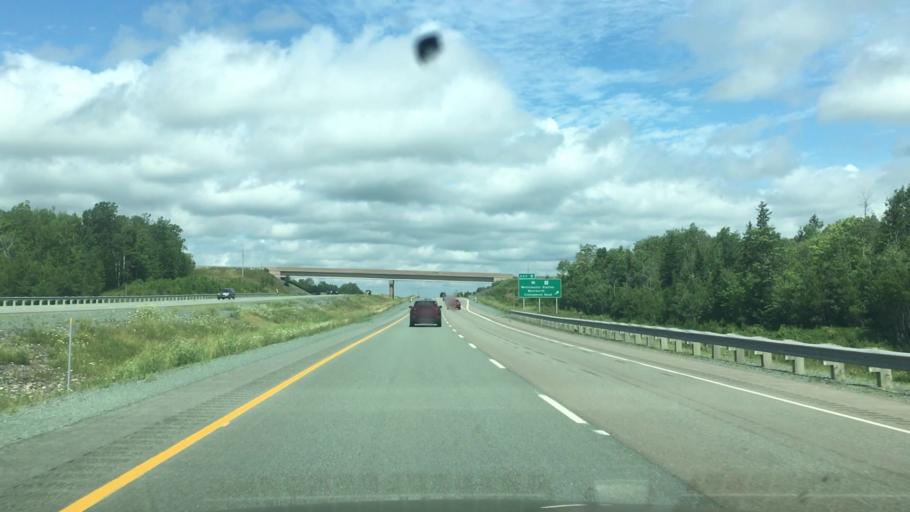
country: CA
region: Nova Scotia
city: Oxford
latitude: 45.6050
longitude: -63.7345
